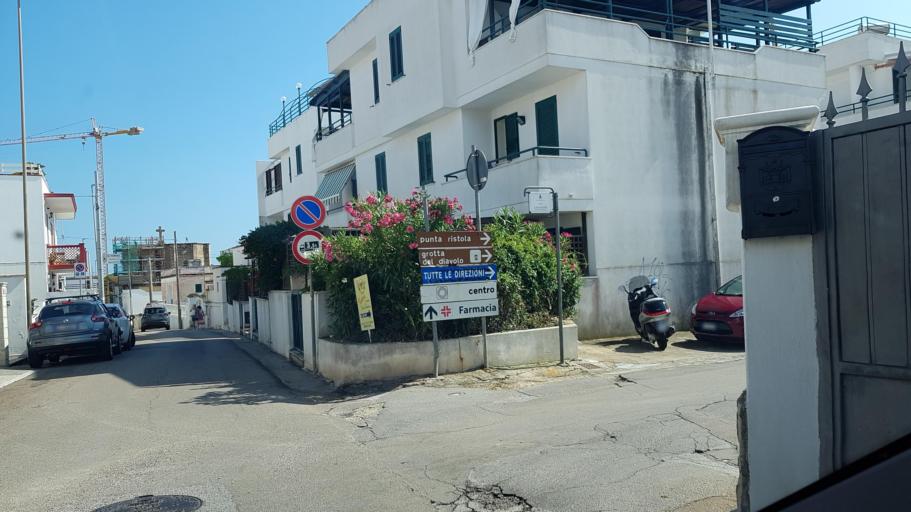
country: IT
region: Apulia
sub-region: Provincia di Lecce
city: Leuca
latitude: 39.7986
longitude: 18.3543
